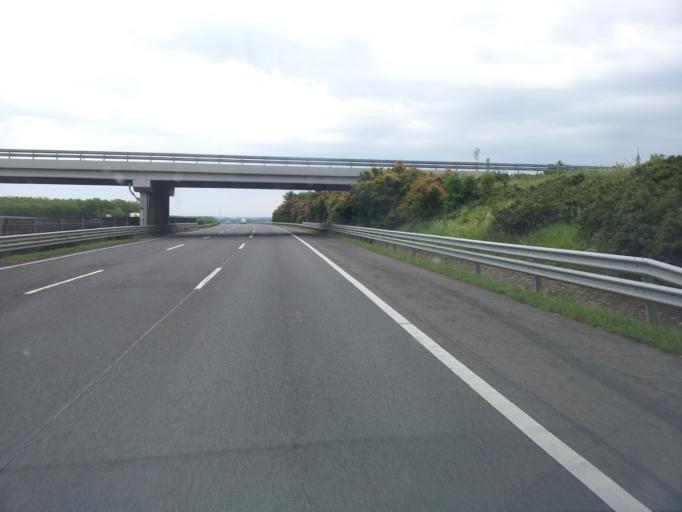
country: HU
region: Heves
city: Hatvan
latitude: 47.6838
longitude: 19.7152
